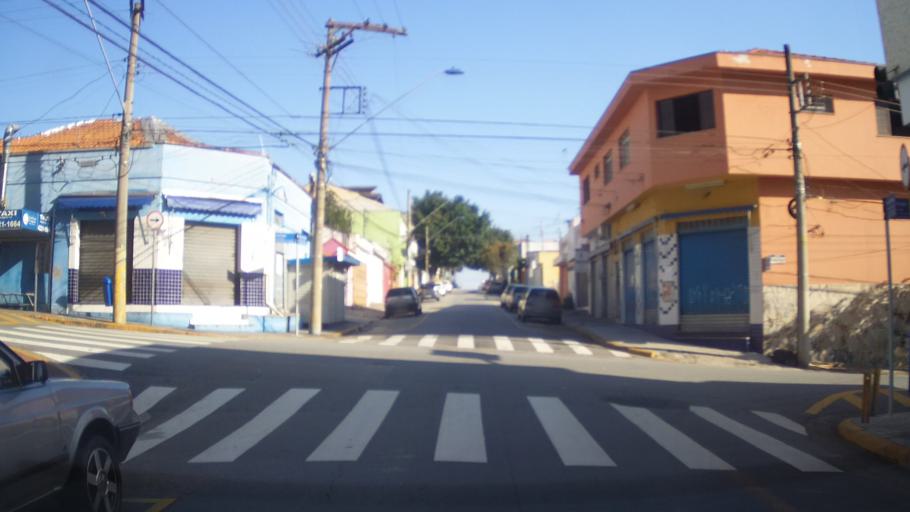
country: BR
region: Sao Paulo
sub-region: Sao Caetano Do Sul
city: Sao Caetano do Sul
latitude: -23.6239
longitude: -46.5657
